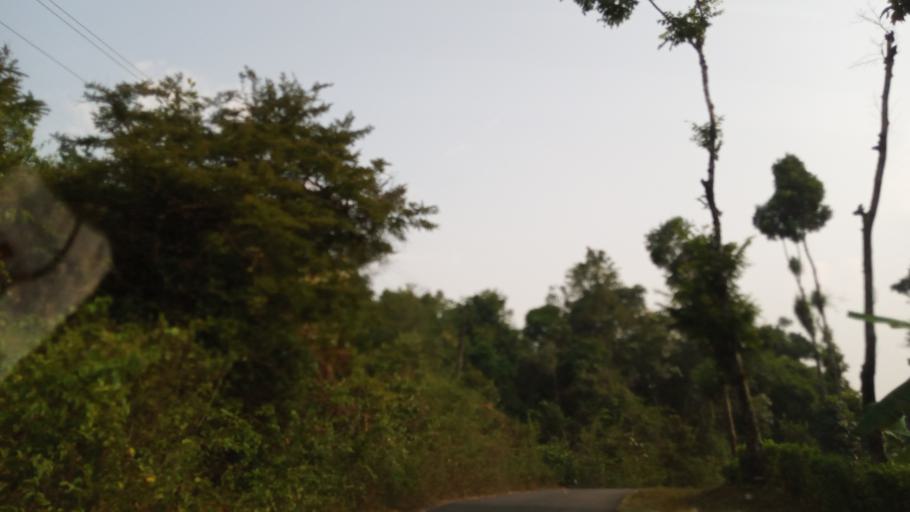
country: IN
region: Karnataka
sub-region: Chikmagalur
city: Mudigere
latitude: 13.0097
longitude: 75.6284
